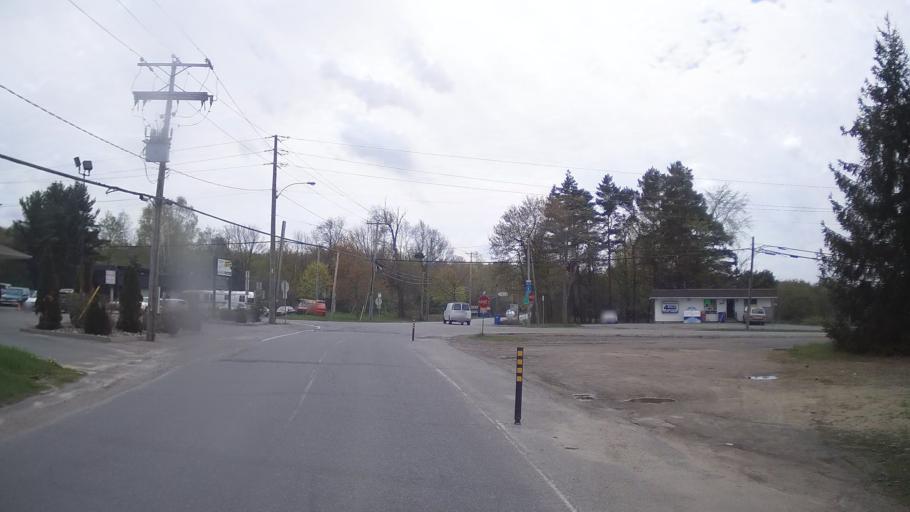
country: CA
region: Quebec
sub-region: Monteregie
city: Hudson
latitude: 45.4466
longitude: -74.1677
